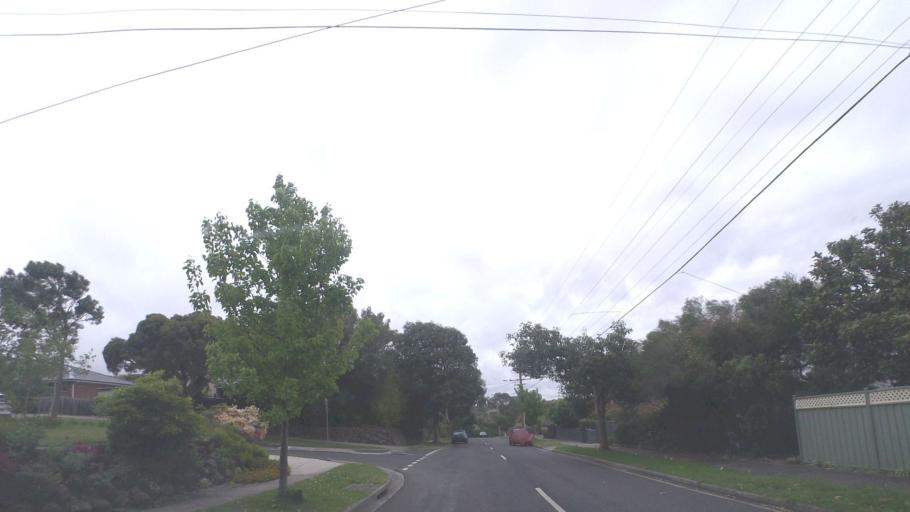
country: AU
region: Victoria
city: Mitcham
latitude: -37.8050
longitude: 145.1971
